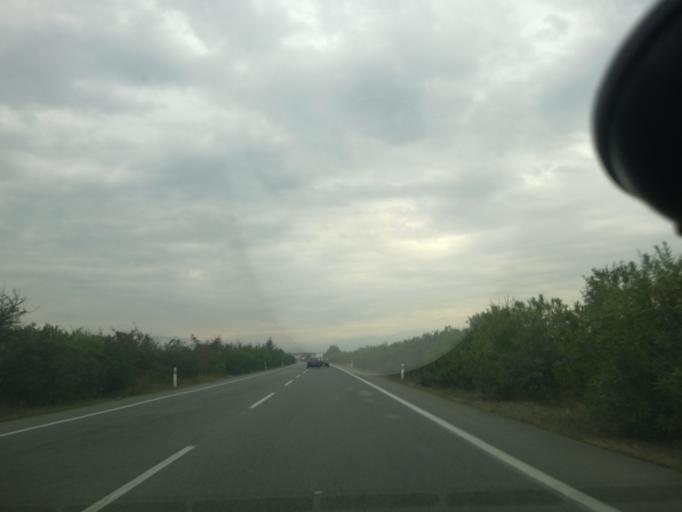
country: GR
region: Central Macedonia
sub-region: Nomos Pellis
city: Mandalo
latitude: 40.8091
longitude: 22.2289
